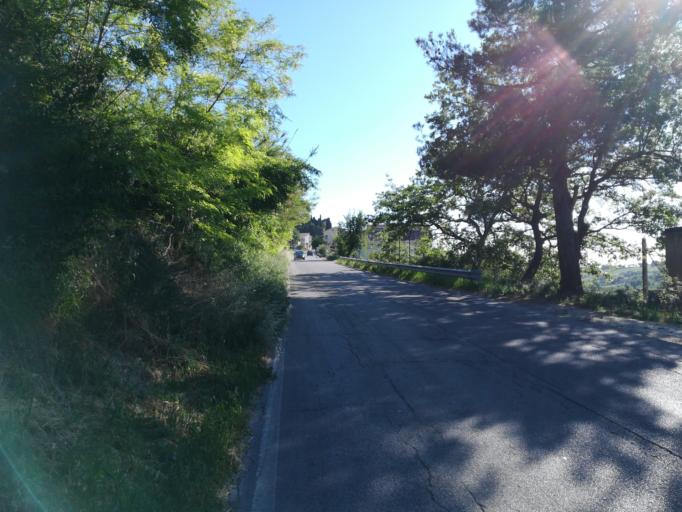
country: IT
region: Abruzzo
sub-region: Provincia di Chieti
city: Bucchianico
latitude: 42.2965
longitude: 14.1718
